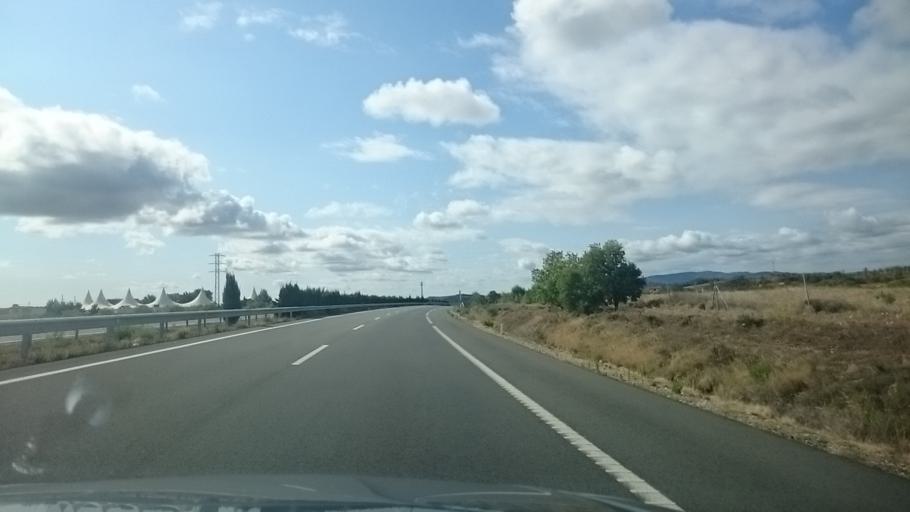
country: ES
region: La Rioja
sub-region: Provincia de La Rioja
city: Calahorra
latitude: 42.3178
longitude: -1.9873
